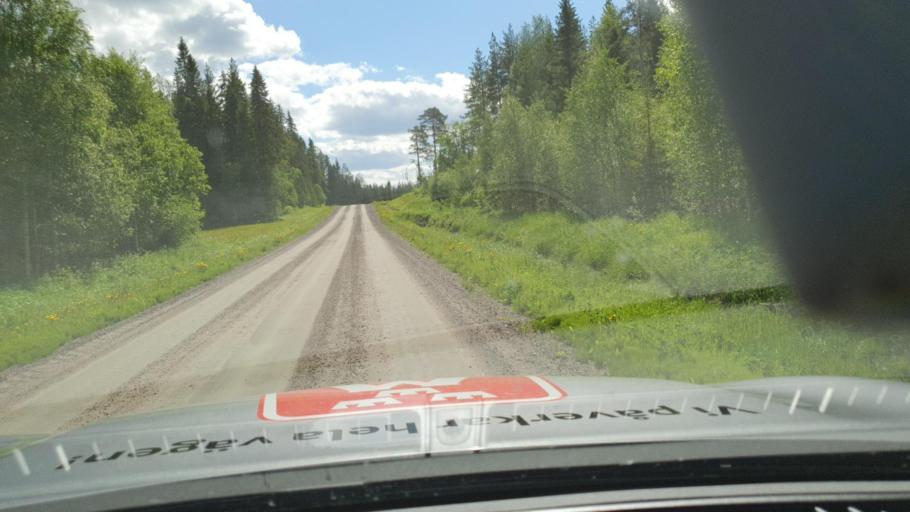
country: SE
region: Norrbotten
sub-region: Pitea Kommun
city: Rosvik
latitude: 65.4940
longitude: 21.6035
